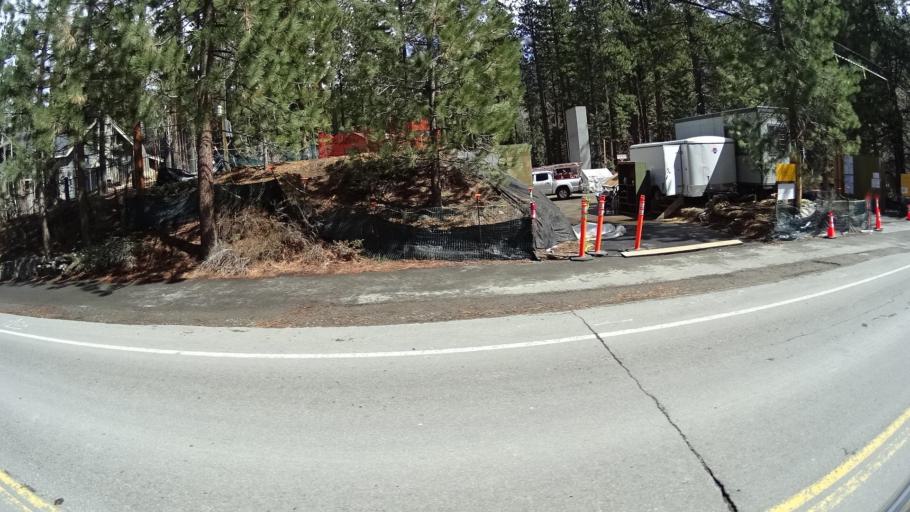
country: US
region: Nevada
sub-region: Washoe County
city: Incline Village
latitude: 39.2357
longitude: -119.9344
